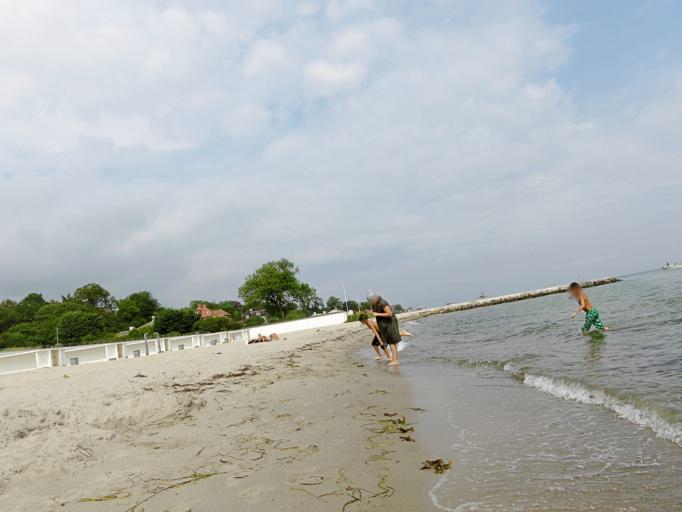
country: DK
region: Capital Region
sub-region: Gentofte Kommune
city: Charlottenlund
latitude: 55.7791
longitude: 12.5929
